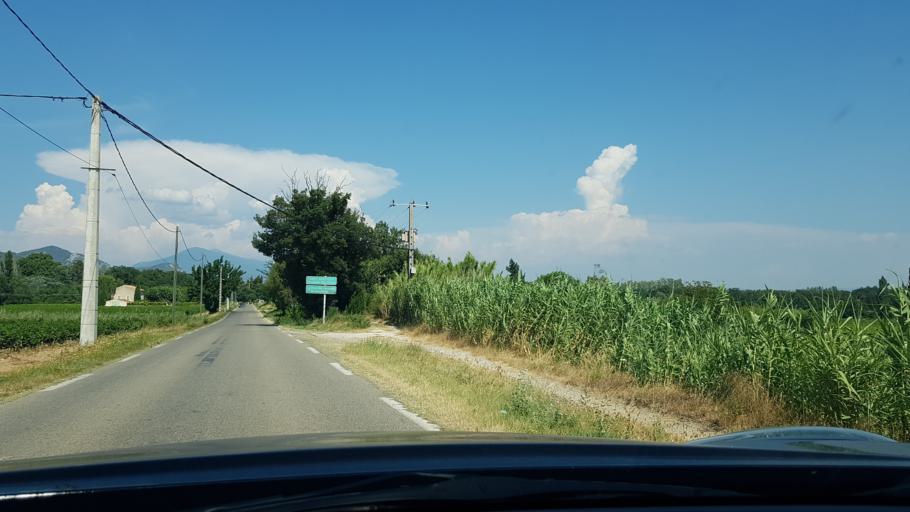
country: FR
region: Provence-Alpes-Cote d'Azur
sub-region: Departement du Vaucluse
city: Beaumes-de-Venise
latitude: 44.1114
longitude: 4.9972
